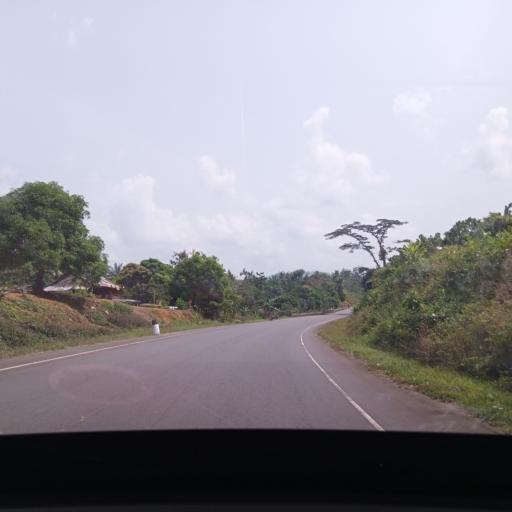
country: LR
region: Margibi
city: Kakata
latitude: 6.2527
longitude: -10.3025
